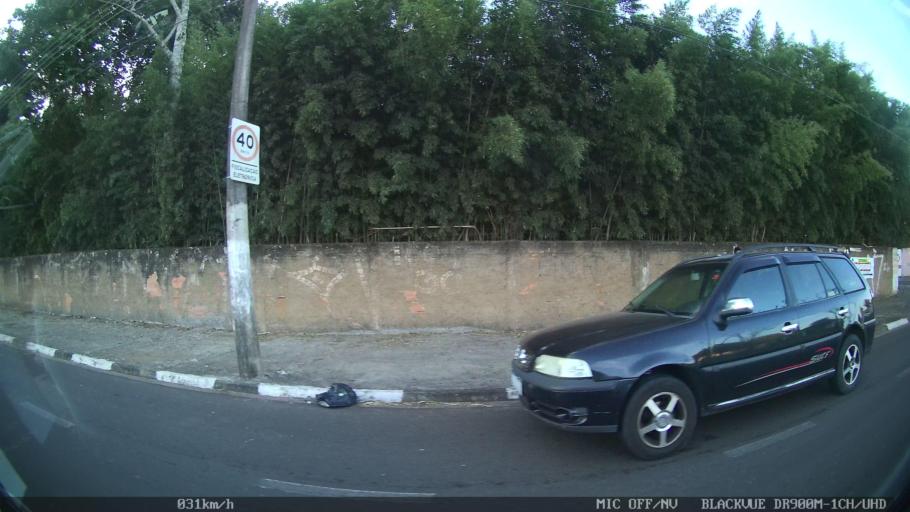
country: BR
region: Sao Paulo
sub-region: Franca
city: Franca
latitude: -20.4928
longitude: -47.3990
